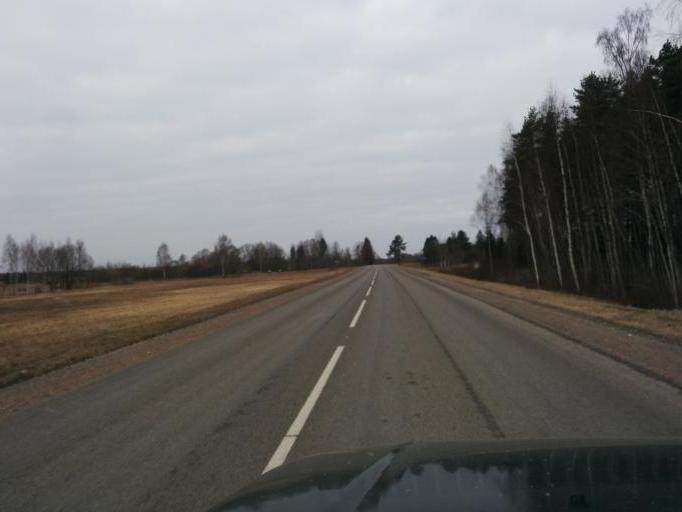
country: LV
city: Tireli
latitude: 56.8318
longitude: 23.5995
